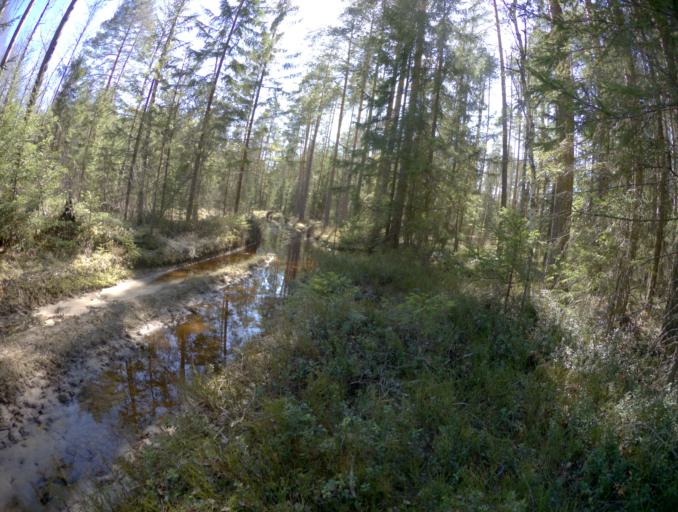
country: RU
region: Vladimir
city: Ivanishchi
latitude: 55.8286
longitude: 40.4247
